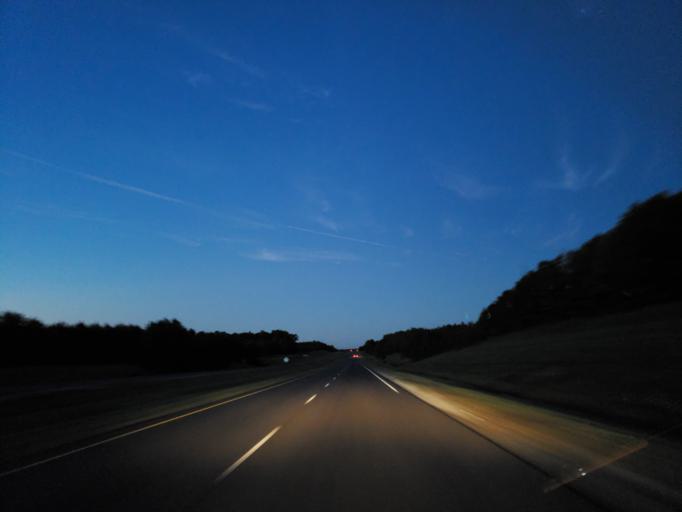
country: US
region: Mississippi
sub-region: Clarke County
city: Quitman
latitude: 32.0132
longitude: -88.6876
